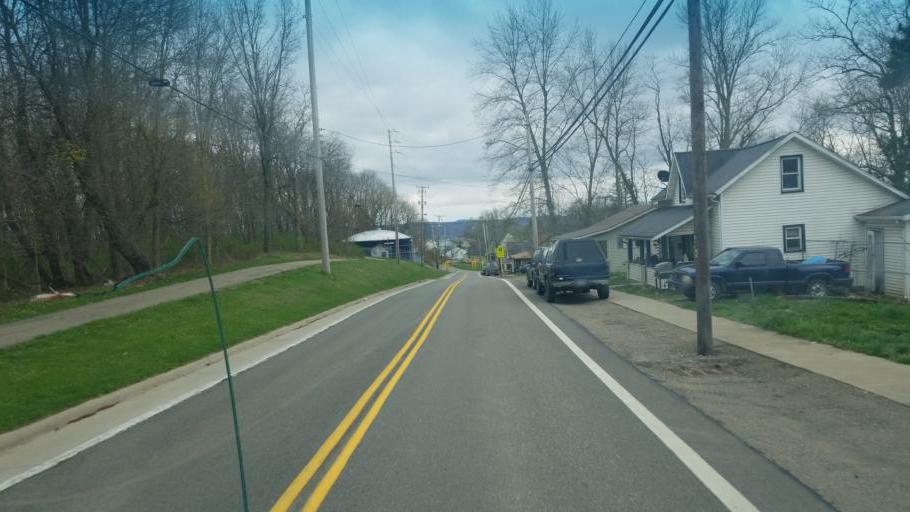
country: US
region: Ohio
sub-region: Holmes County
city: Millersburg
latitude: 40.5584
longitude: -81.9120
